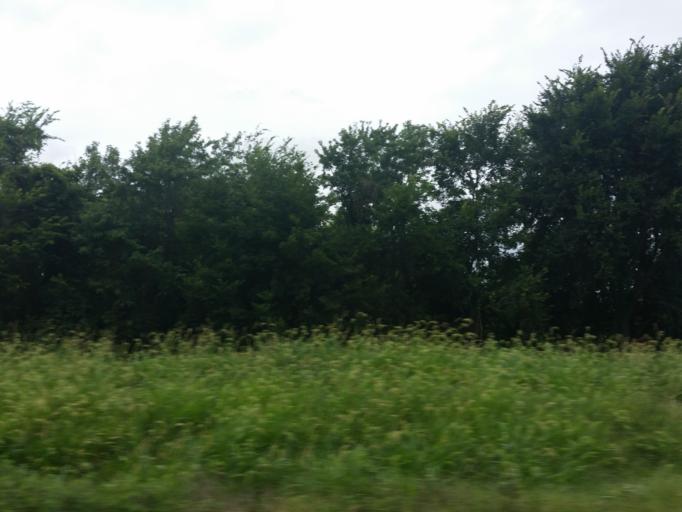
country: US
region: Illinois
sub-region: Alexander County
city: Cairo
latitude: 36.9692
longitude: -89.1515
